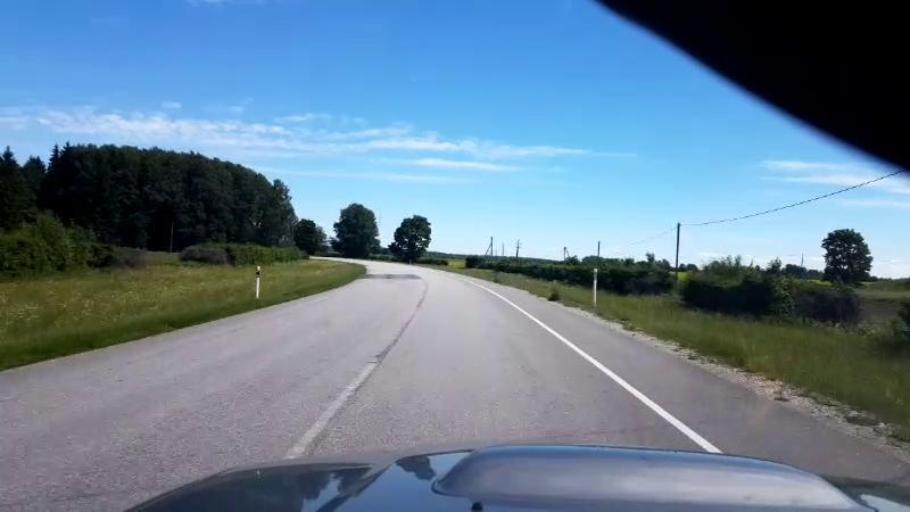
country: EE
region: Jaervamaa
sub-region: Koeru vald
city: Koeru
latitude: 58.9888
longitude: 25.9741
